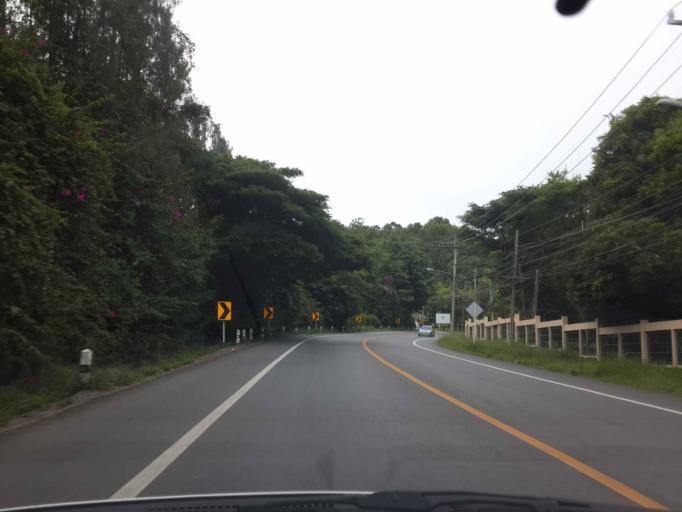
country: TH
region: Chon Buri
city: Si Racha
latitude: 13.2225
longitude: 100.9659
